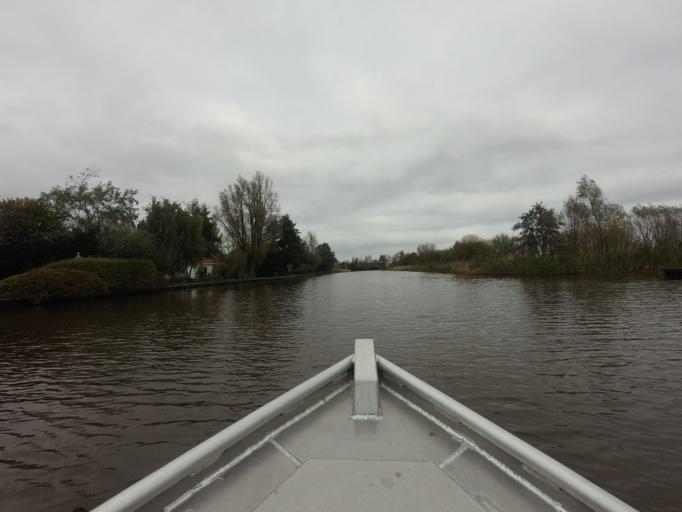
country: NL
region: Overijssel
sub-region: Gemeente Steenwijkerland
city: Blokzijl
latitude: 52.7509
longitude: 5.9950
